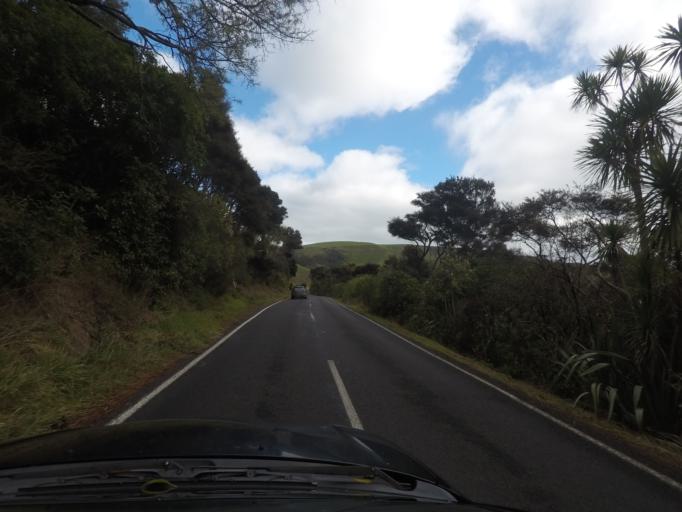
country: NZ
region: Auckland
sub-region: Auckland
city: Muriwai Beach
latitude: -36.8771
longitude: 174.4544
